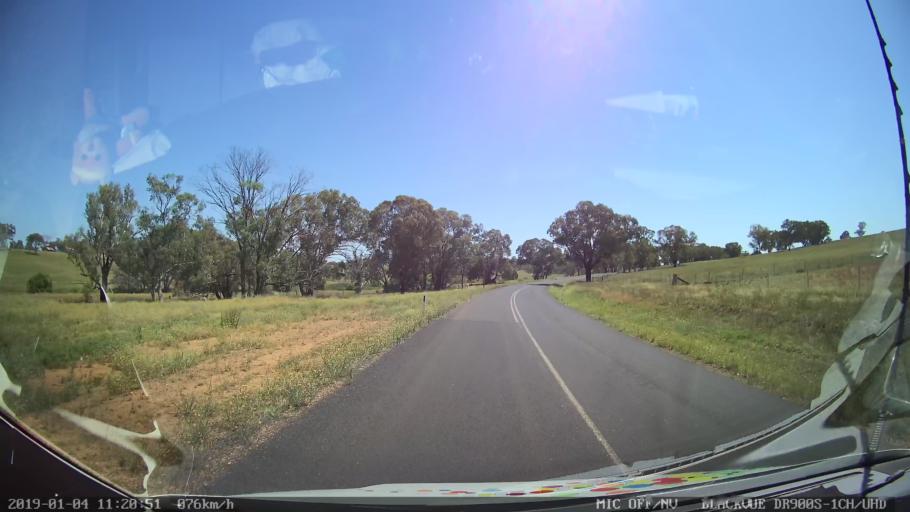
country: AU
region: New South Wales
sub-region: Cabonne
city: Molong
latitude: -33.1595
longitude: 148.7058
